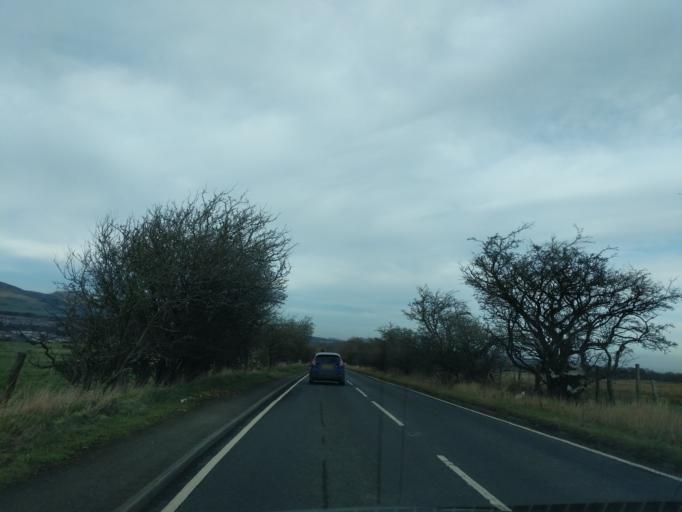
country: GB
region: Scotland
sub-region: Midlothian
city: Penicuik
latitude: 55.8234
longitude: -3.2024
